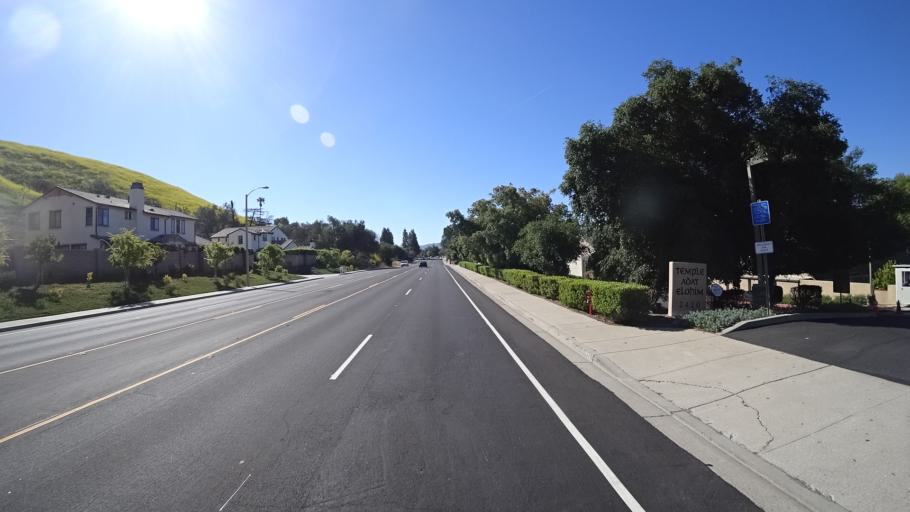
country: US
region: California
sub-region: Ventura County
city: Thousand Oaks
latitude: 34.1785
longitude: -118.8402
